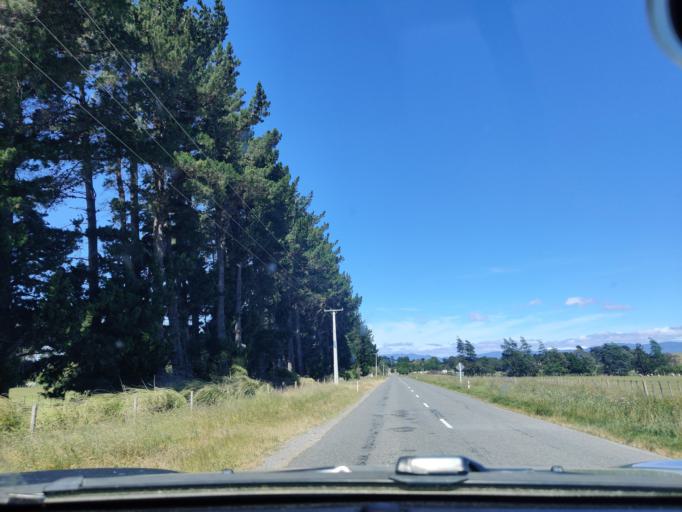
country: NZ
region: Wellington
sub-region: South Wairarapa District
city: Waipawa
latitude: -41.2252
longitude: 175.3508
